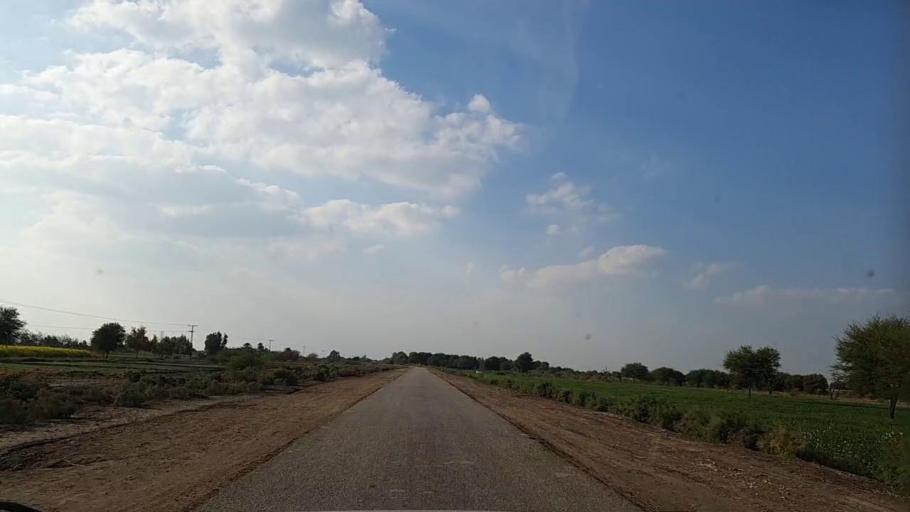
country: PK
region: Sindh
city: Pithoro
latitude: 25.6674
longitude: 69.2367
